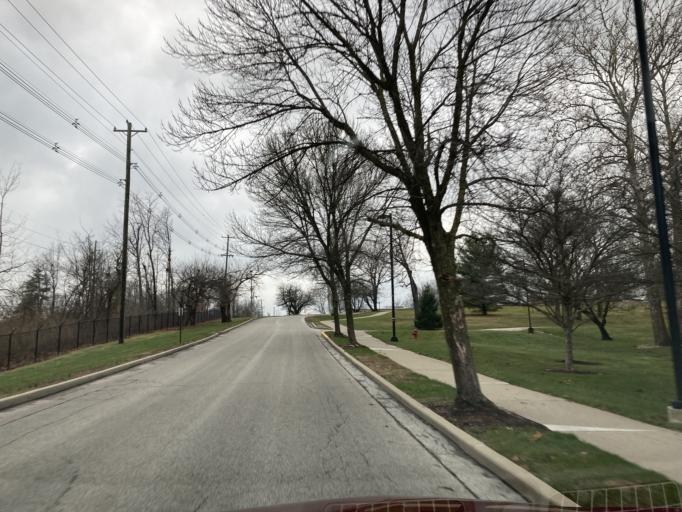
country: US
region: Indiana
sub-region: Monroe County
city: Bloomington
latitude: 39.1730
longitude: -86.5131
